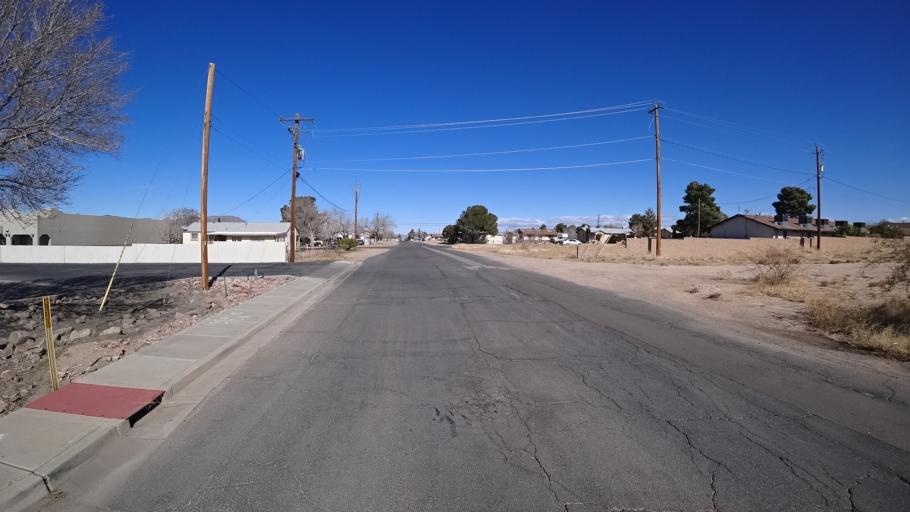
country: US
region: Arizona
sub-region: Mohave County
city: Kingman
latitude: 35.1916
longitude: -114.0225
